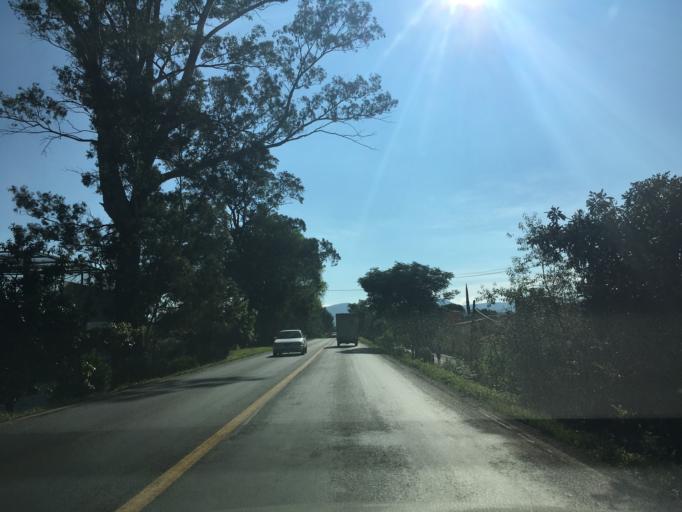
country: MX
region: Mexico
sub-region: Chalco
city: Chilchota
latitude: 19.8503
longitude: -102.1180
